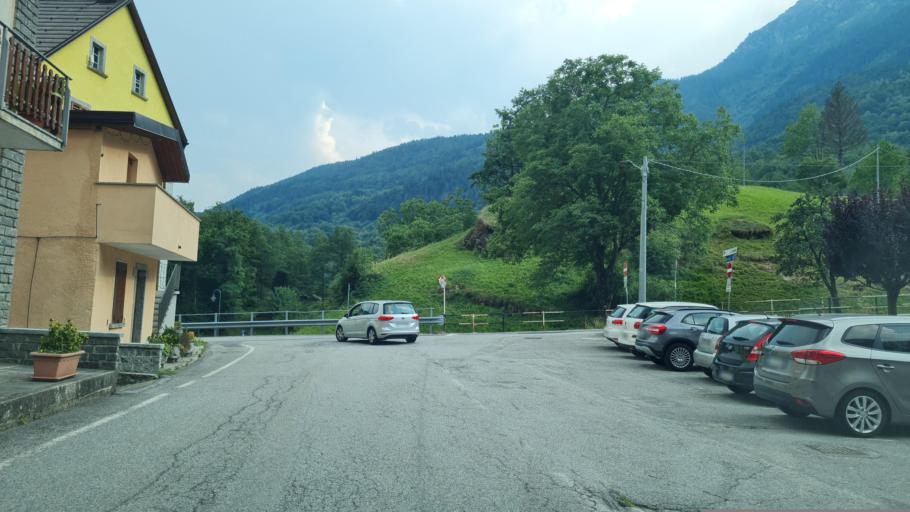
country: IT
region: Piedmont
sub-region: Provincia Verbano-Cusio-Ossola
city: Baceno
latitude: 46.2720
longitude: 8.3051
